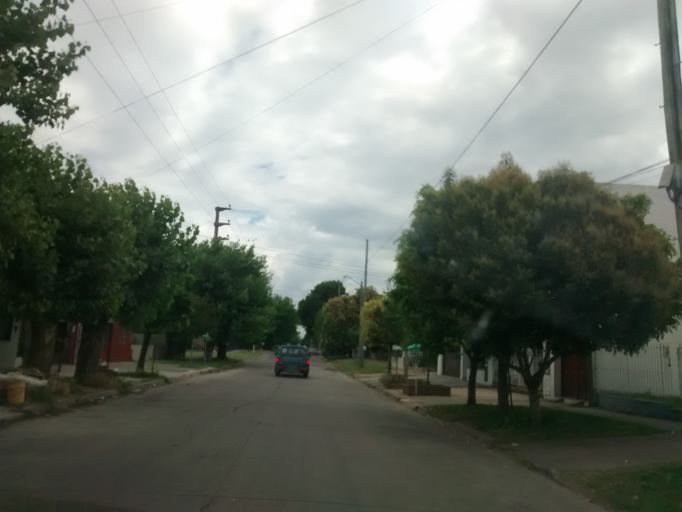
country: AR
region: Buenos Aires
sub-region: Partido de La Plata
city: La Plata
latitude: -34.9229
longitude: -57.9149
